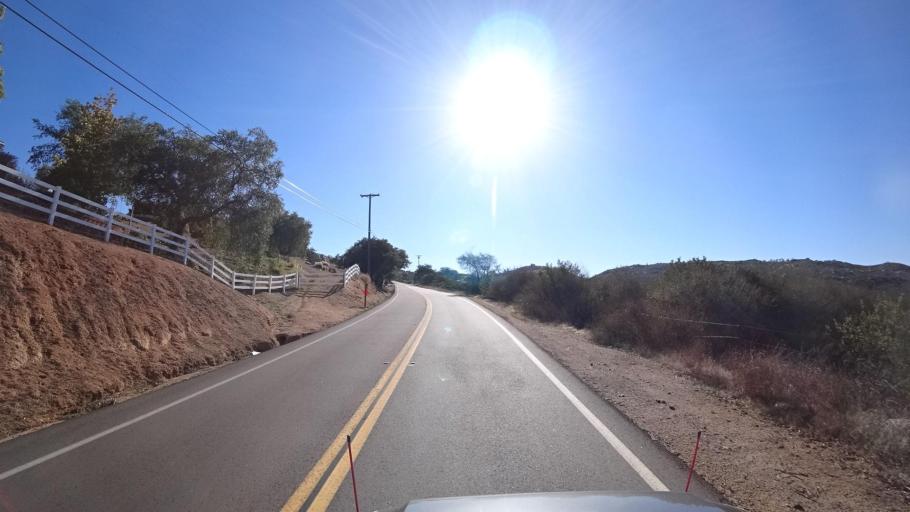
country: US
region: California
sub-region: San Diego County
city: Jamul
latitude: 32.6778
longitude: -116.7460
